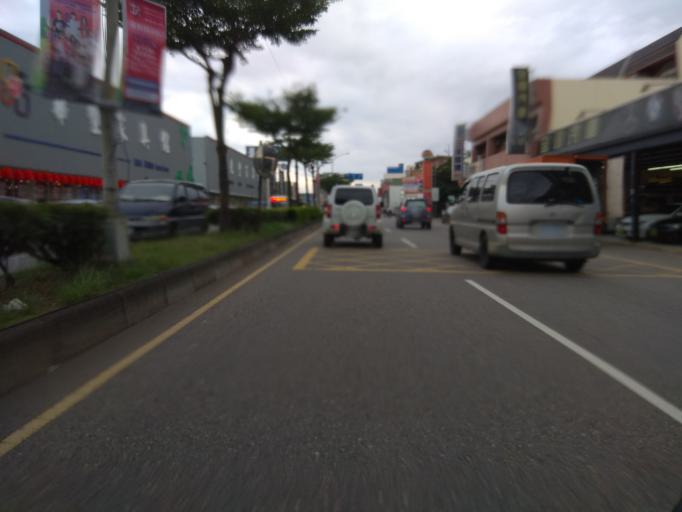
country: TW
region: Taiwan
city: Daxi
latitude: 24.9308
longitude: 121.2141
